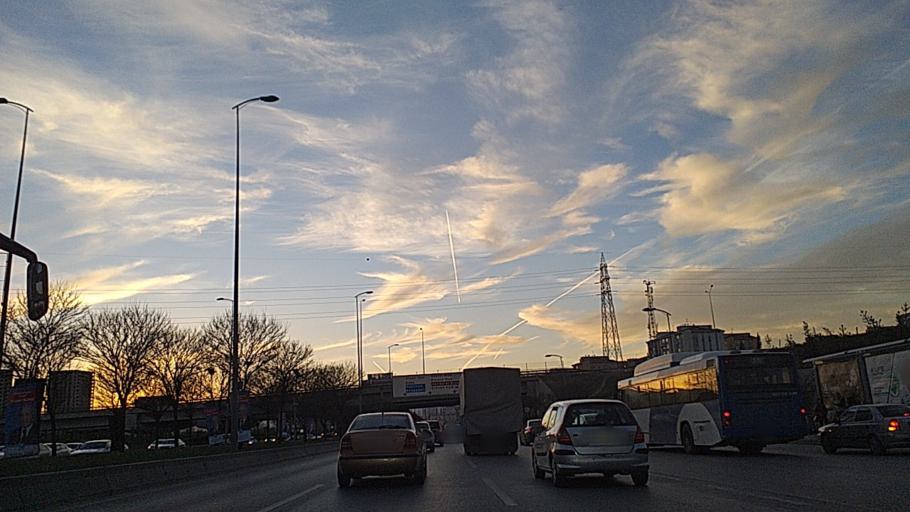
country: TR
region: Ankara
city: Etimesgut
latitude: 39.9666
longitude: 32.6317
